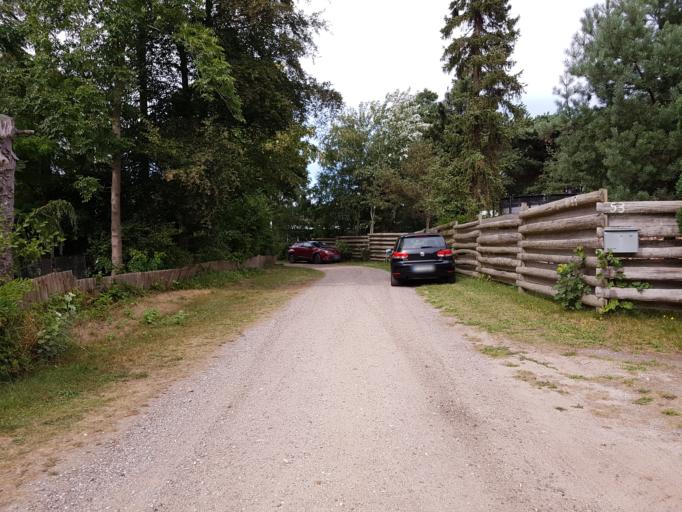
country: DK
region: Zealand
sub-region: Guldborgsund Kommune
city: Nykobing Falster
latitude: 54.5952
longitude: 11.9682
